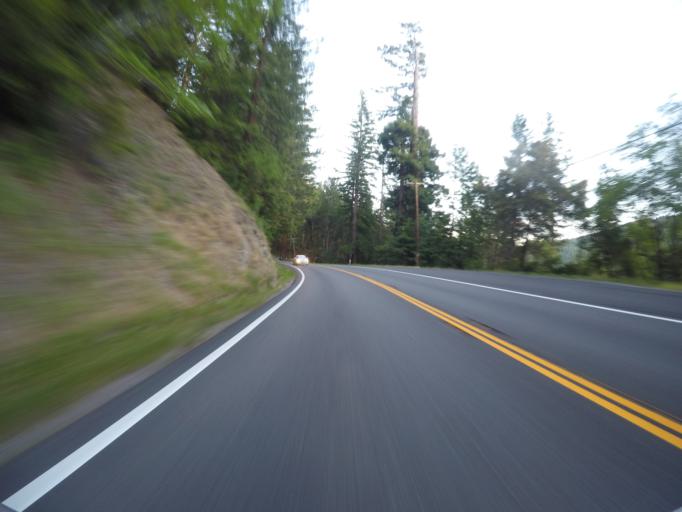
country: US
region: California
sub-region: Humboldt County
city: Redway
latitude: 39.9141
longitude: -123.7603
